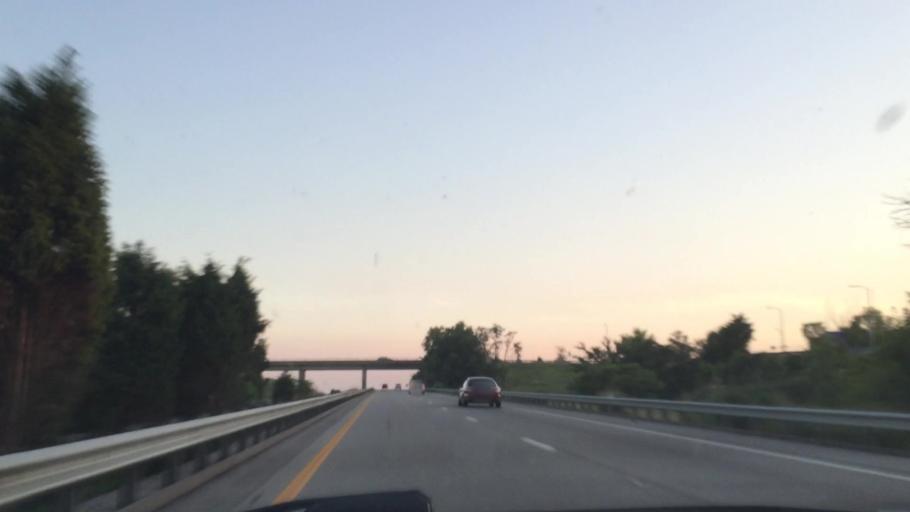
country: US
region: Kentucky
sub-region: Trimble County
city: Providence
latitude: 38.5226
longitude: -85.2332
